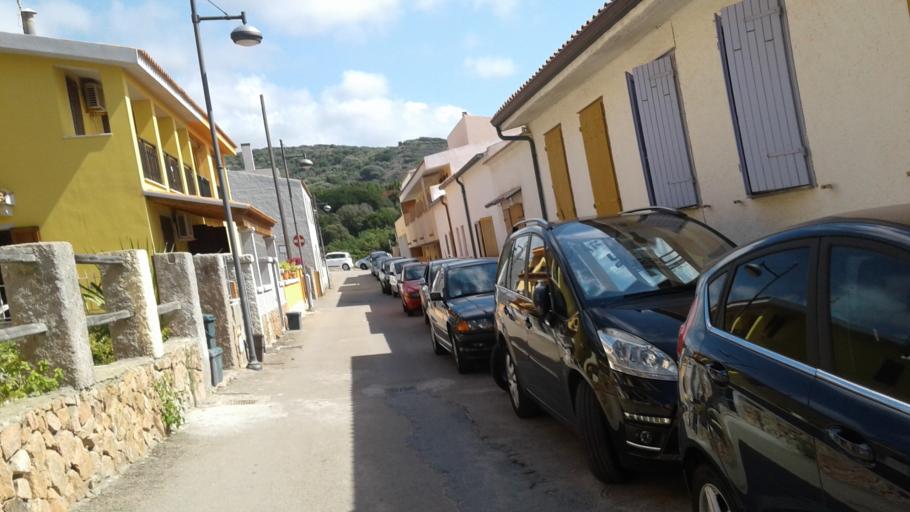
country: IT
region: Sardinia
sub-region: Provincia di Olbia-Tempio
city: Trinita d'Agultu
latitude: 41.0108
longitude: 8.8775
